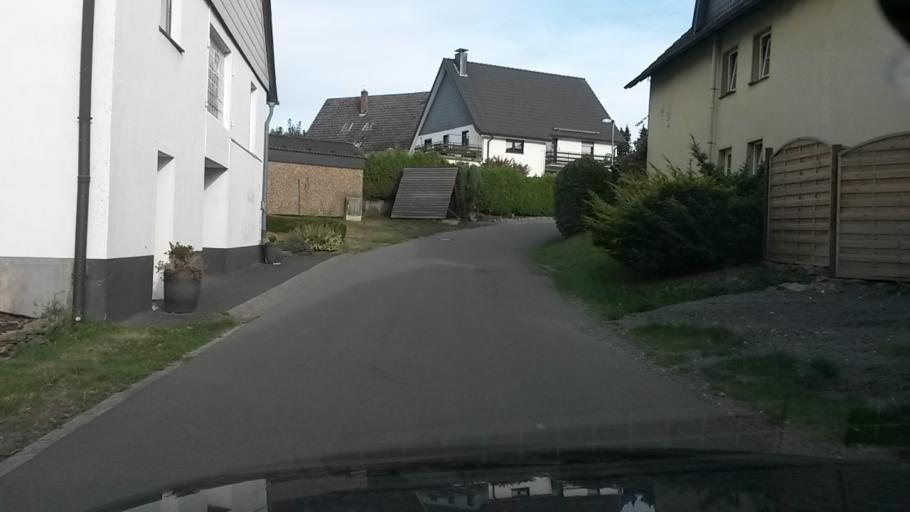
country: DE
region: North Rhine-Westphalia
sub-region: Regierungsbezirk Arnsberg
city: Herscheid
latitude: 51.2132
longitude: 7.7572
